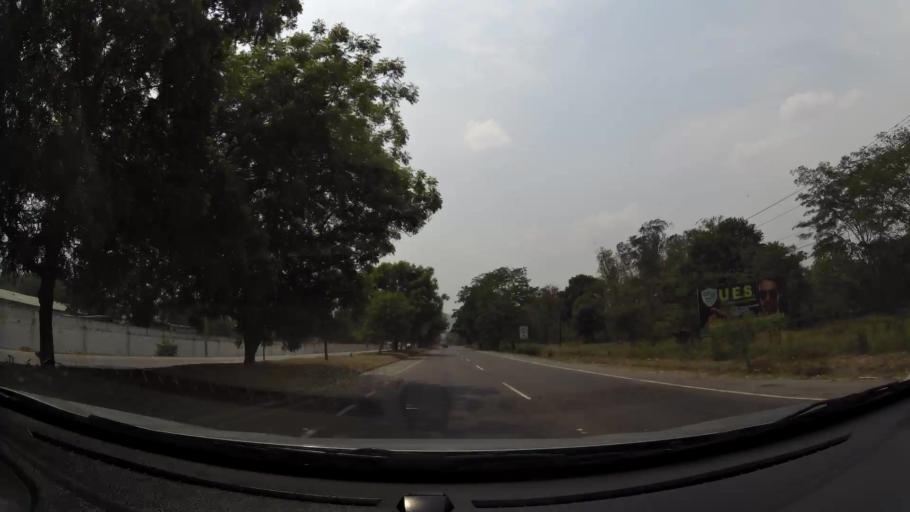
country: HN
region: Cortes
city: Chotepe
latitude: 15.3998
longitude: -87.9988
